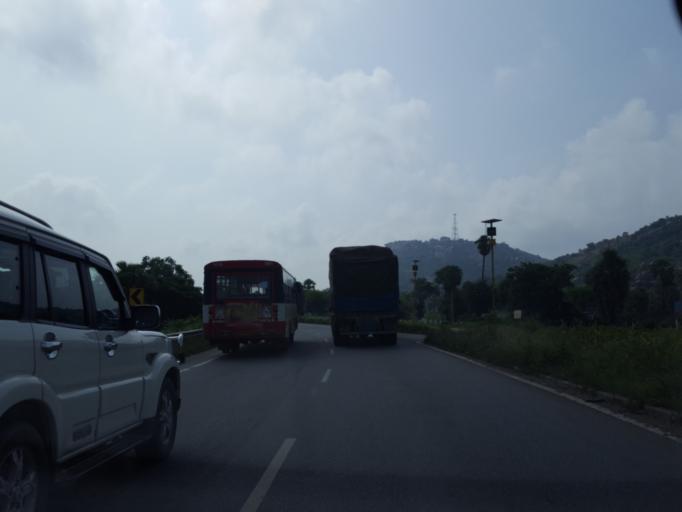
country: IN
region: Telangana
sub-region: Rangareddi
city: Ghatkesar
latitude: 17.2964
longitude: 78.7407
